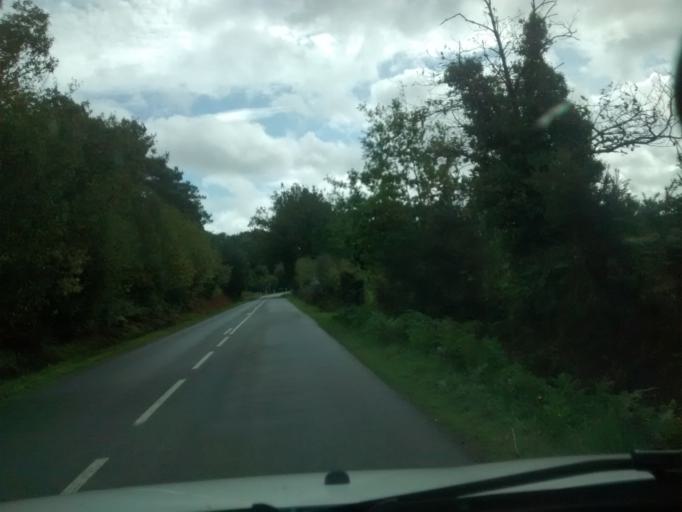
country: FR
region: Brittany
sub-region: Departement d'Ille-et-Vilaine
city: Chateaubourg
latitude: 48.1439
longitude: -1.4018
